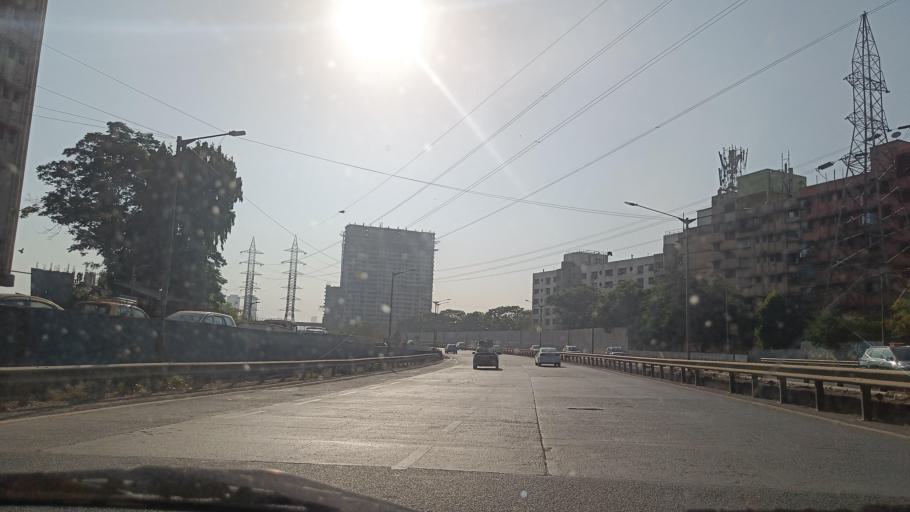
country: IN
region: Maharashtra
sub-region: Mumbai Suburban
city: Mumbai
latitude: 19.0335
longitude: 72.8999
